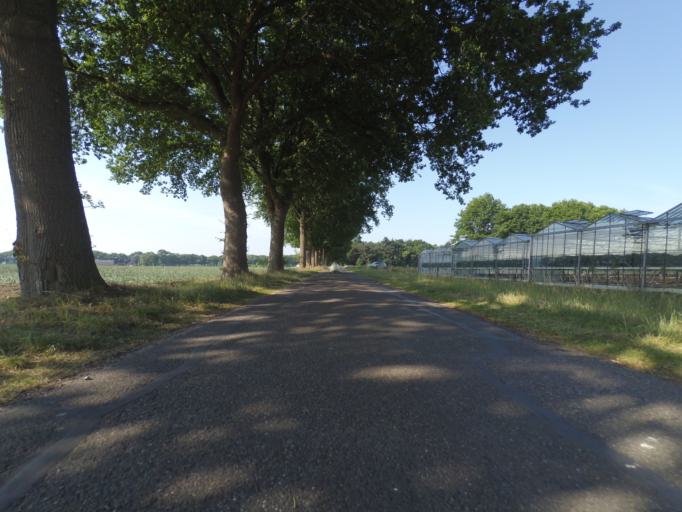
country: BE
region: Flanders
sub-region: Provincie Antwerpen
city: Essen
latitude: 51.4384
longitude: 4.3888
